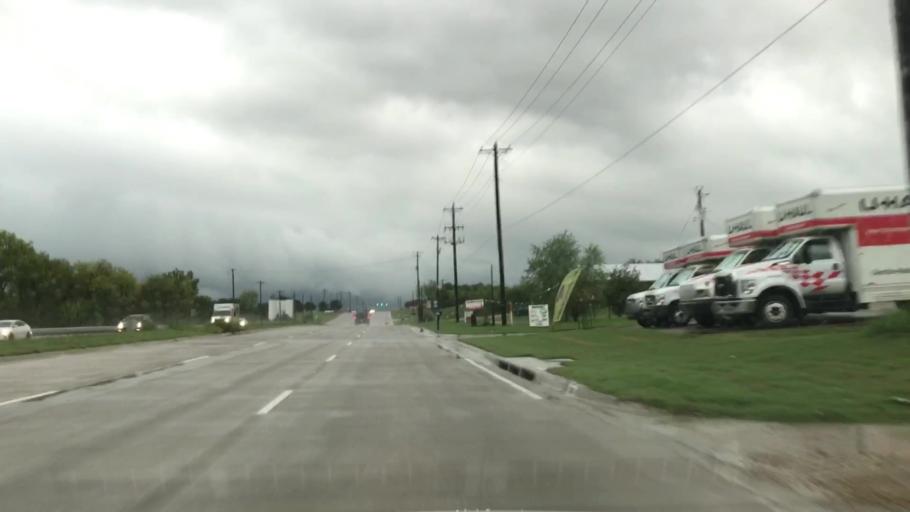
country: US
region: Texas
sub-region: Collin County
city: Lavon
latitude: 33.0219
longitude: -96.4631
